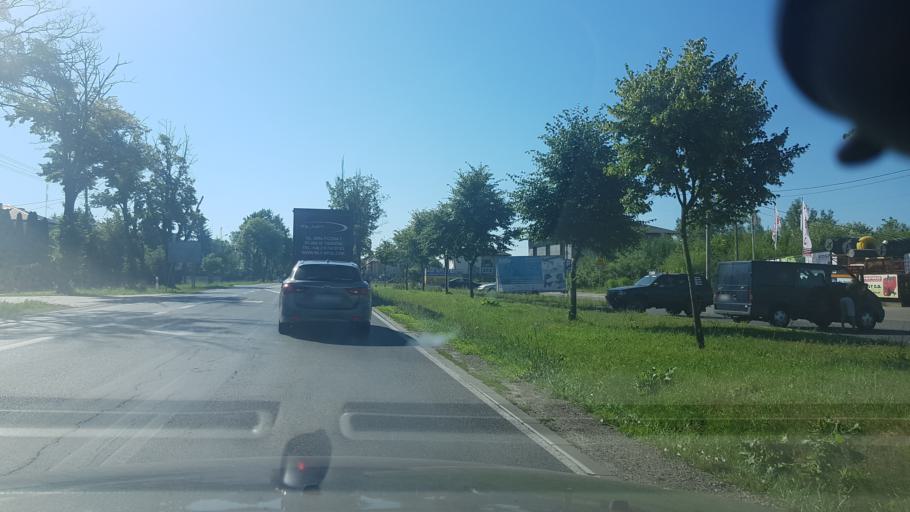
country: PL
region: Masovian Voivodeship
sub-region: Powiat wegrowski
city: Lochow
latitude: 52.5294
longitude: 21.6833
